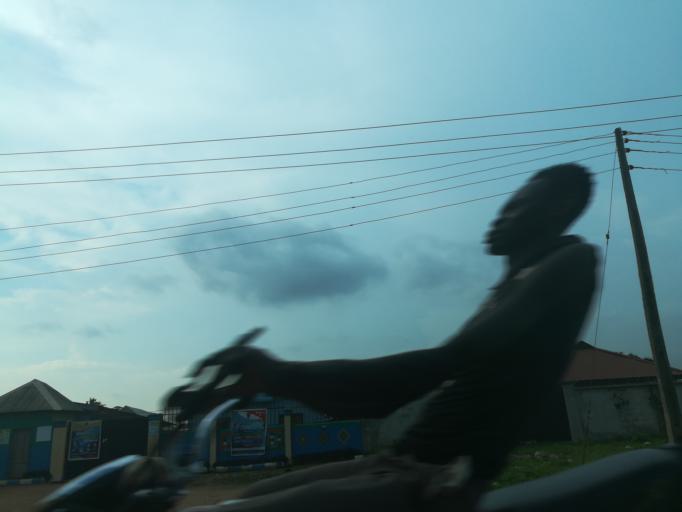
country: NG
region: Lagos
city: Ikorodu
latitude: 6.6124
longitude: 3.5981
